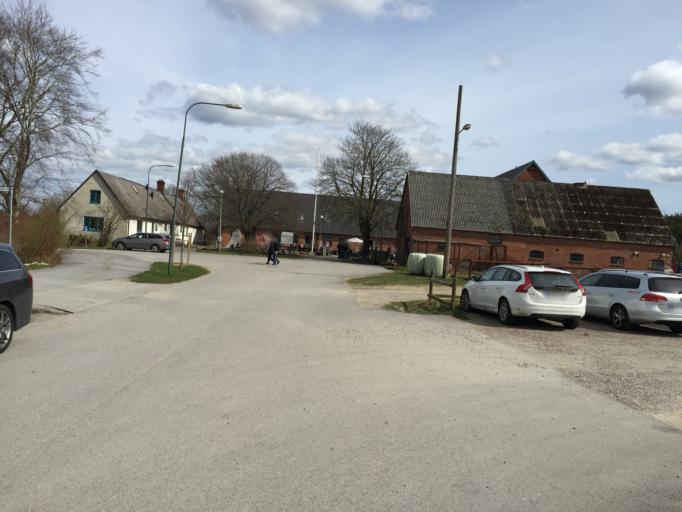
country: SE
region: Skane
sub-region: Lunds Kommun
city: Veberod
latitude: 55.6270
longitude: 13.5013
